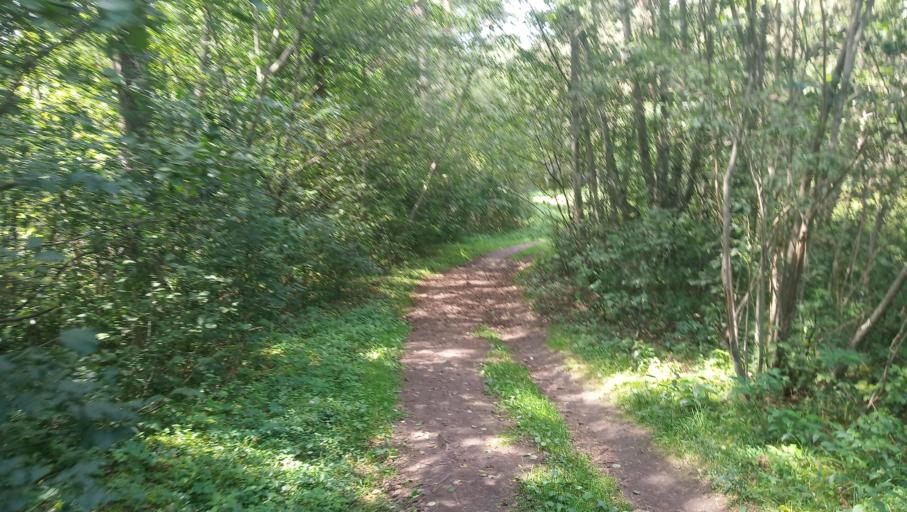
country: BY
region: Minsk
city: Radashkovichy
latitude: 54.2011
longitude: 27.3867
